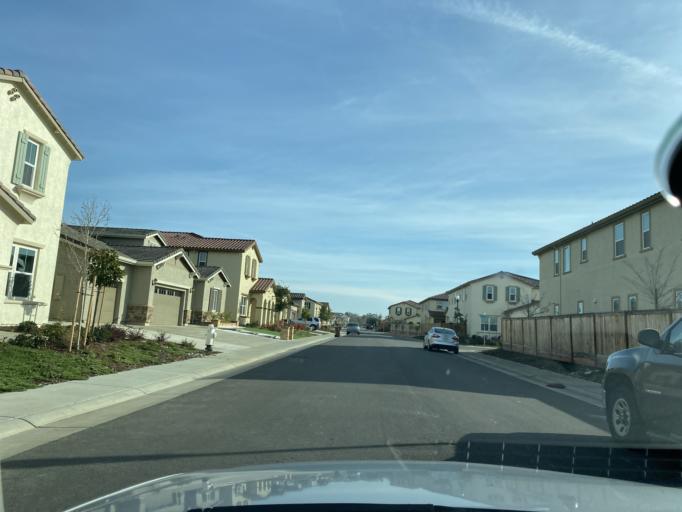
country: US
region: California
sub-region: Sacramento County
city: Elk Grove
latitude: 38.3925
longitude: -121.3873
